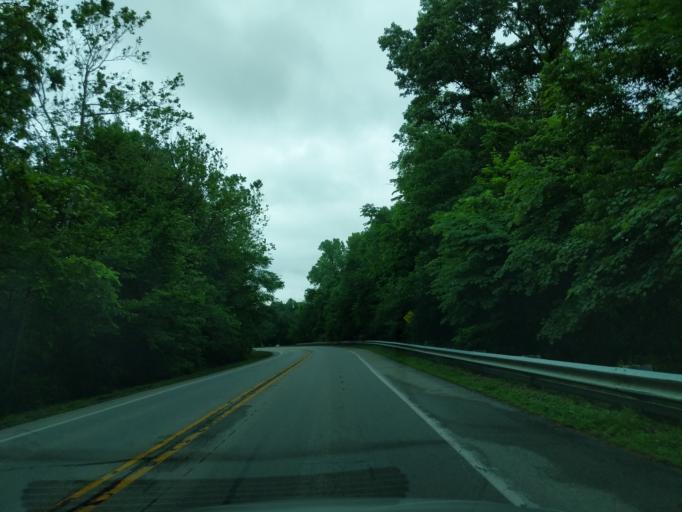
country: US
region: Indiana
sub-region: Hamilton County
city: Noblesville
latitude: 40.0673
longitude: -86.0157
